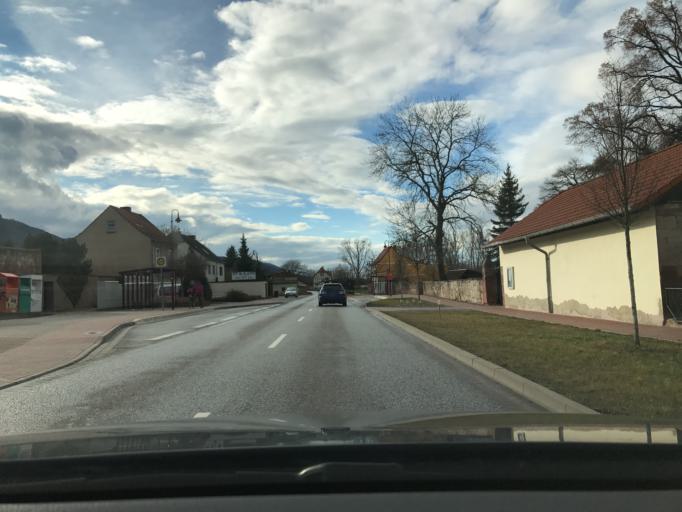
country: DE
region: Saxony-Anhalt
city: Bennungen
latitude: 51.4208
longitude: 11.1412
